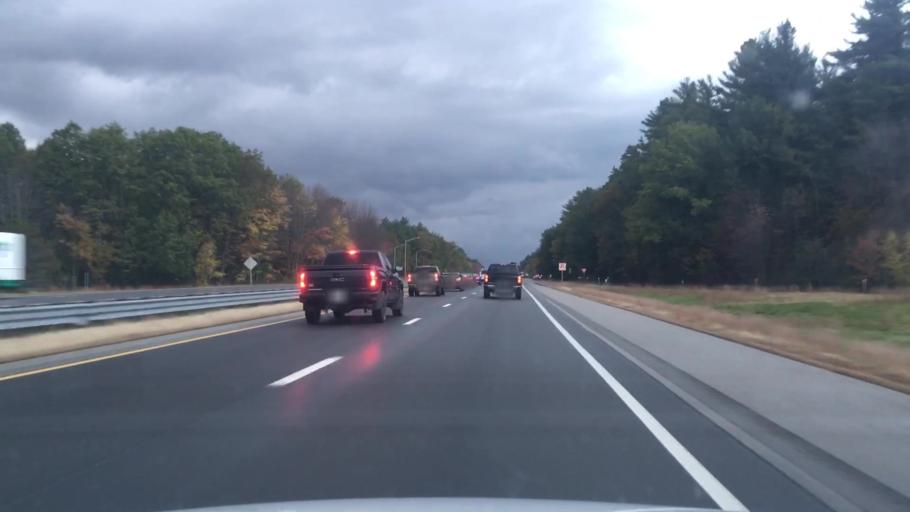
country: US
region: New Hampshire
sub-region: Merrimack County
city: East Concord
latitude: 43.2378
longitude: -71.5394
